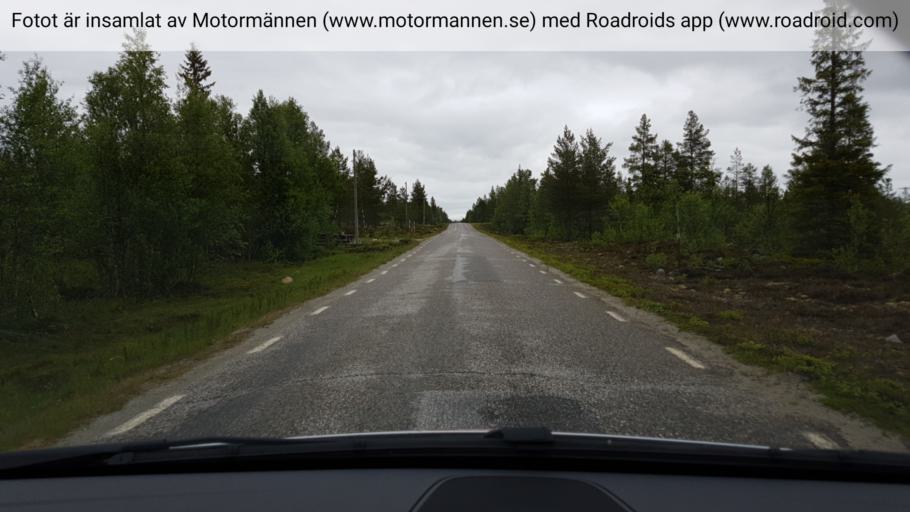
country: SE
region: Jaemtland
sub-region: Harjedalens Kommun
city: Sveg
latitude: 62.2993
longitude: 13.4035
